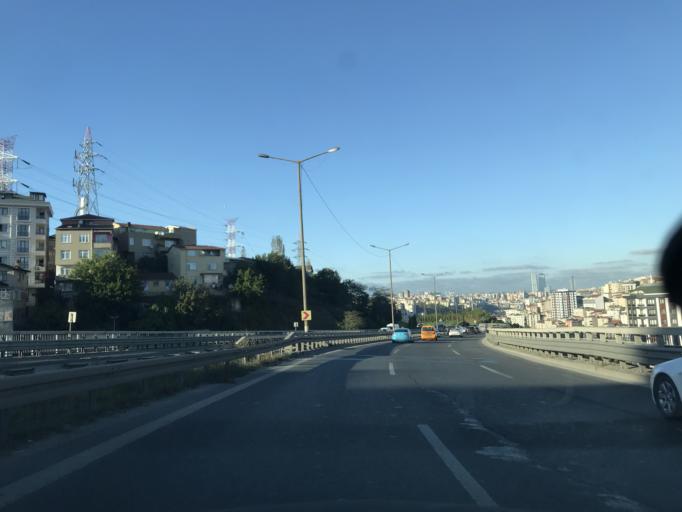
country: TR
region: Istanbul
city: Sisli
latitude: 41.0588
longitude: 28.9570
